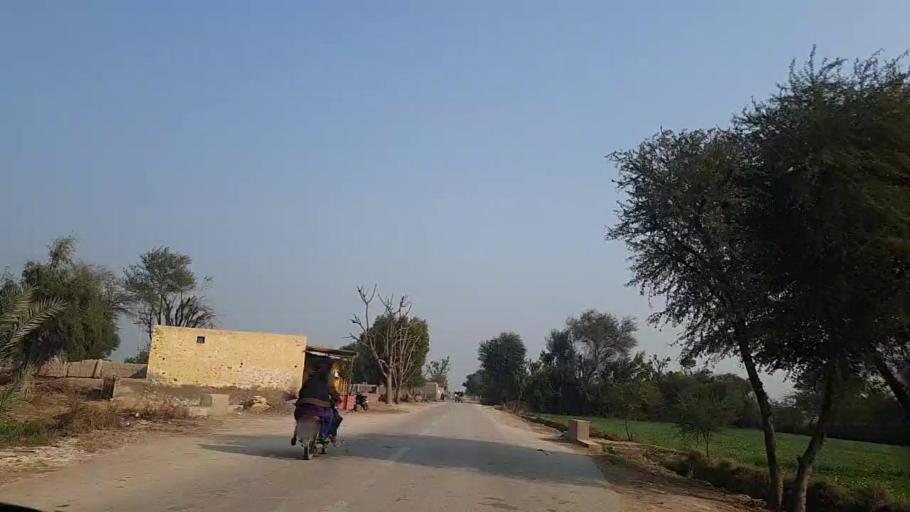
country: PK
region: Sindh
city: Sann
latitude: 26.1432
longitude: 68.1497
